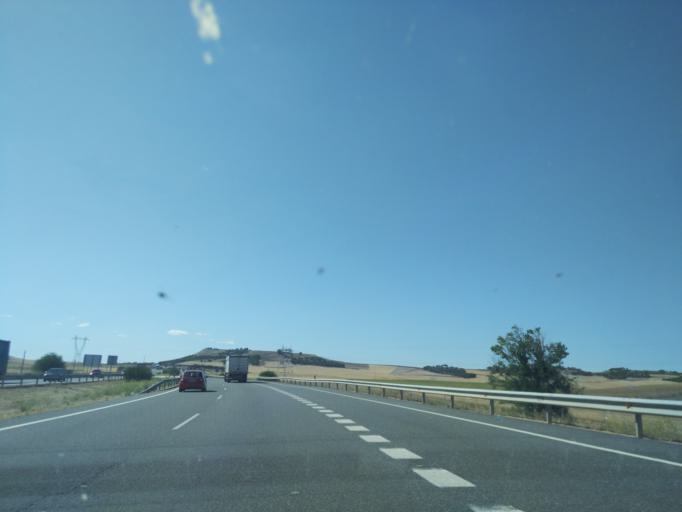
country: ES
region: Castille and Leon
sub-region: Provincia de Valladolid
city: Vega de Valdetronco
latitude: 41.5991
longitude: -5.1248
